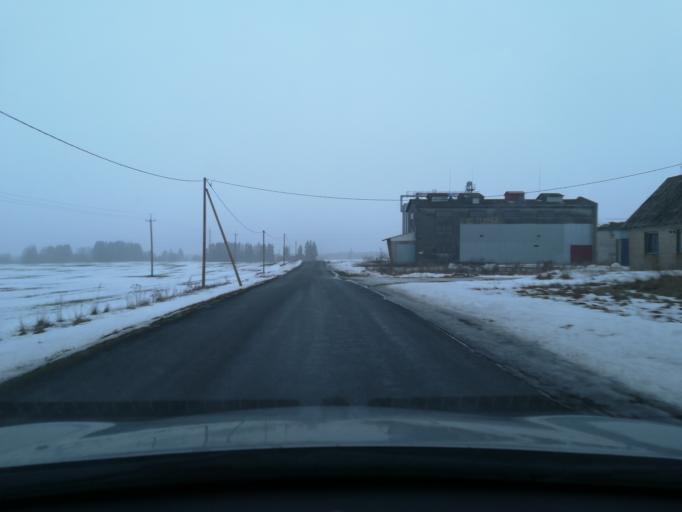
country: EE
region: Harju
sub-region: Raasiku vald
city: Raasiku
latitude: 59.3570
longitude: 25.2021
